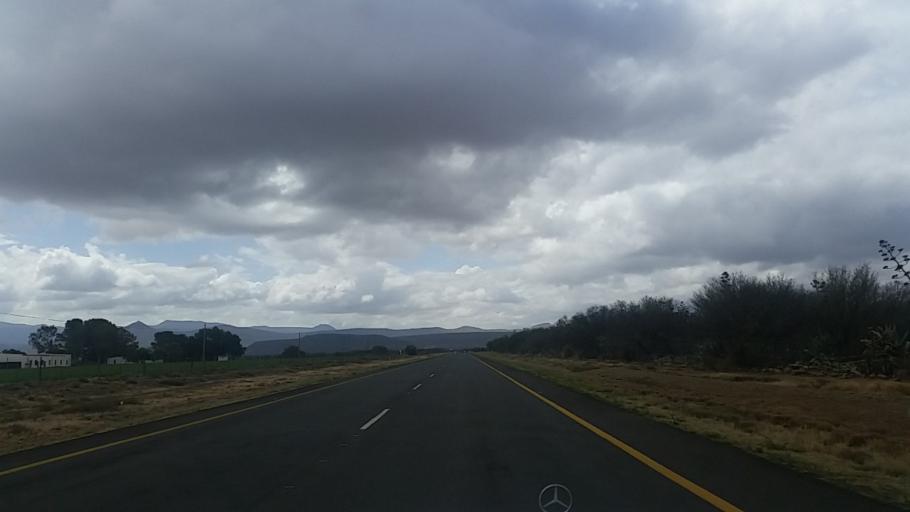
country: ZA
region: Eastern Cape
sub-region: Cacadu District Municipality
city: Graaff-Reinet
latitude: -32.1896
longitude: 24.5581
